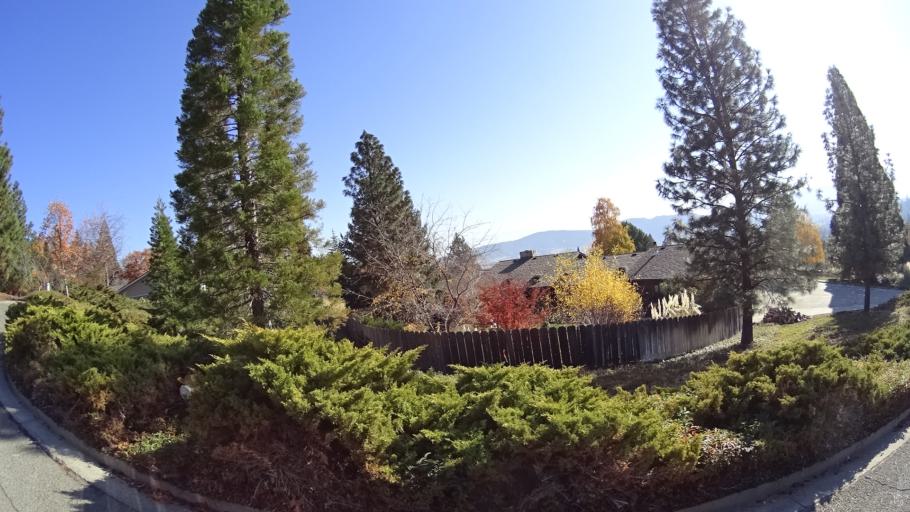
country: US
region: California
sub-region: Siskiyou County
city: Yreka
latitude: 41.7408
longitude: -122.6597
